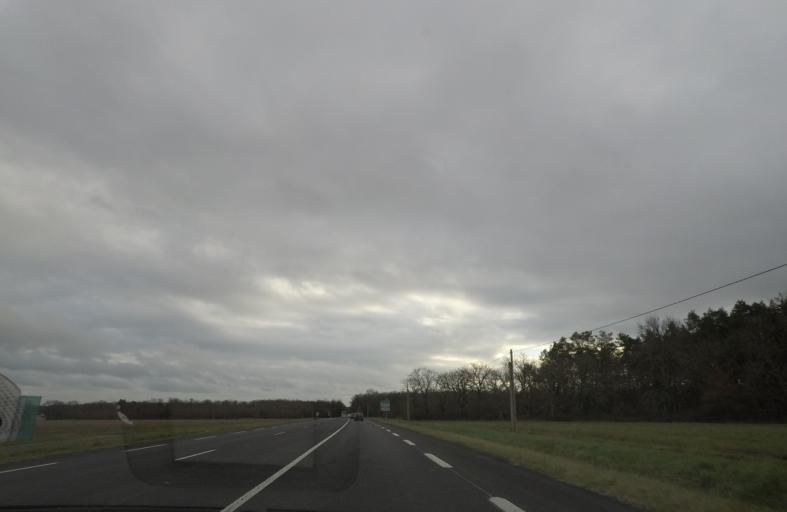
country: FR
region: Centre
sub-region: Departement du Loir-et-Cher
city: Soings-en-Sologne
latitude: 47.4405
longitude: 1.5478
